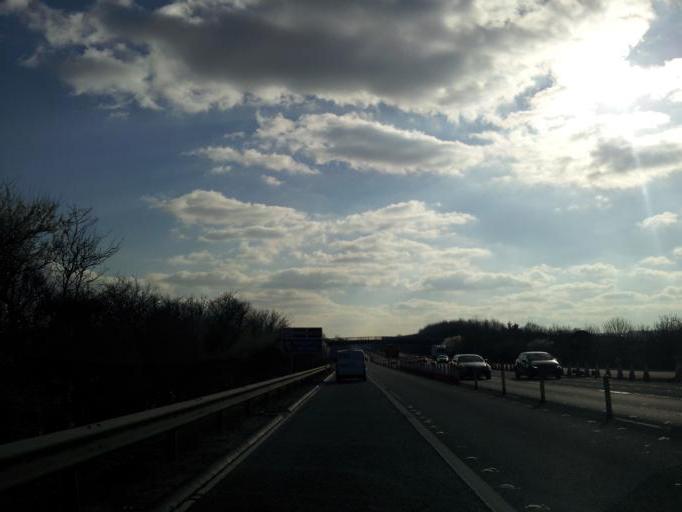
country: GB
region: England
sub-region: Somerset
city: Bridgwater
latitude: 51.1089
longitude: -2.9860
